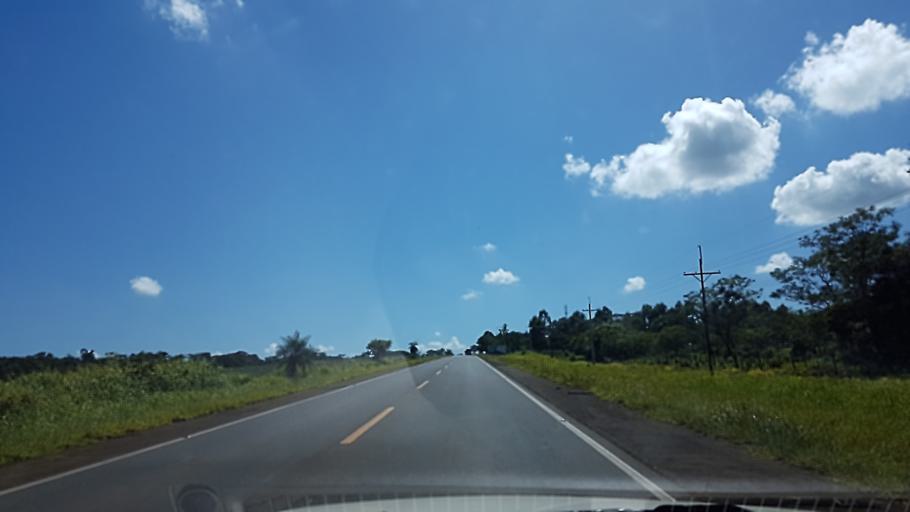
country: PY
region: Itapua
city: Carmen del Parana
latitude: -27.2083
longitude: -56.0765
